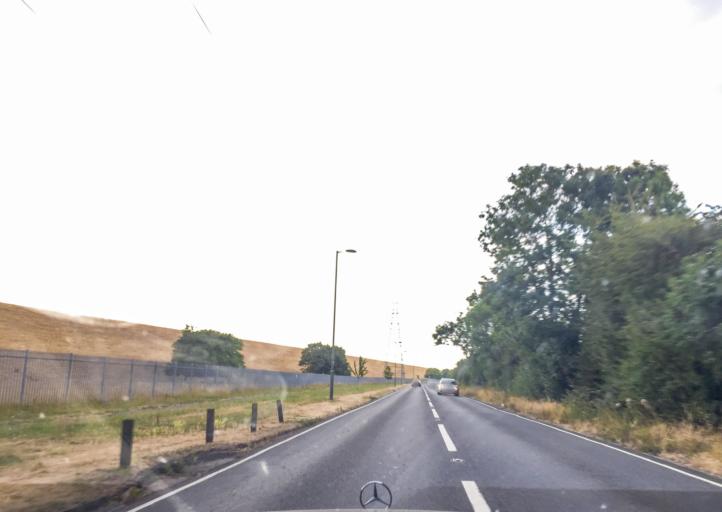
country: GB
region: England
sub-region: Surrey
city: Staines
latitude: 51.4473
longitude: -0.4963
